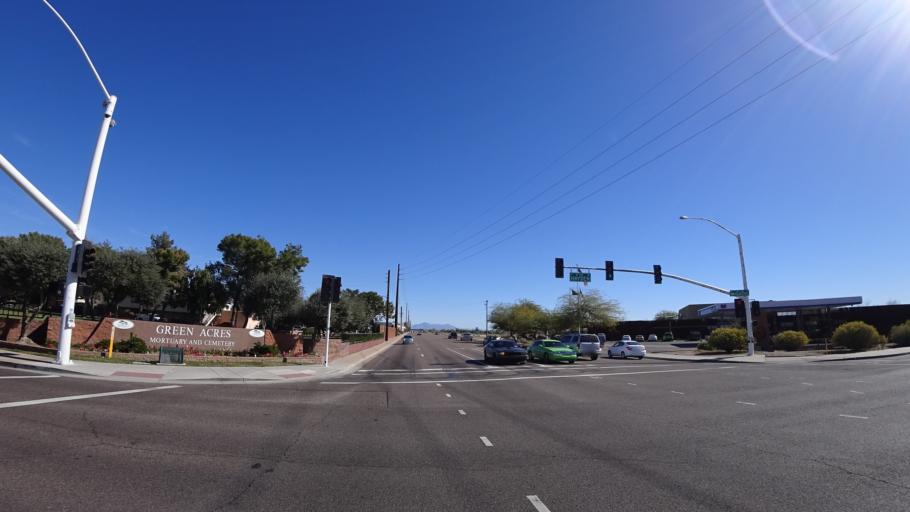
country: US
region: Arizona
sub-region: Maricopa County
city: Tempe
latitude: 33.4514
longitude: -111.9092
